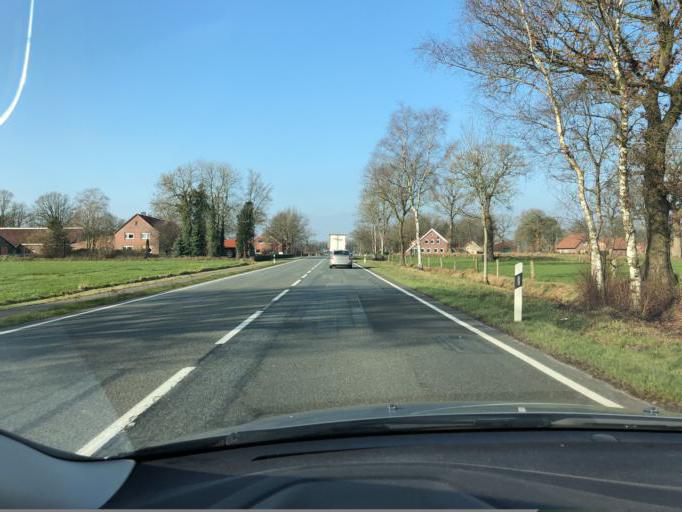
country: DE
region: Lower Saxony
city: Apen
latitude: 53.3016
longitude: 7.7901
